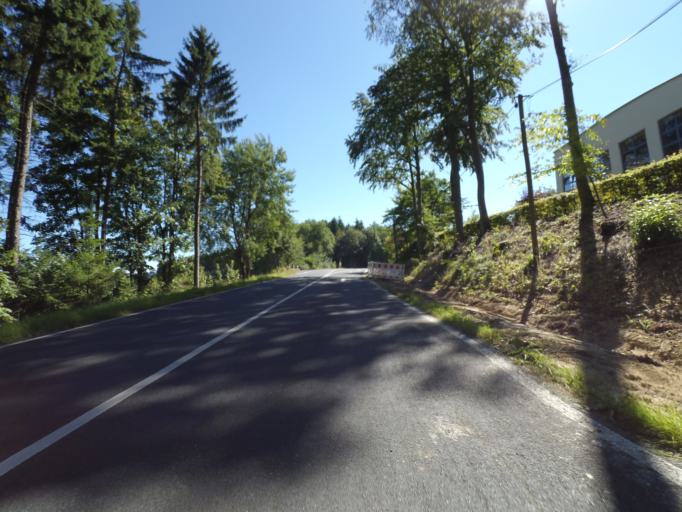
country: DE
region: Rheinland-Pfalz
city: Gefell
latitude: 50.2178
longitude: 6.9162
